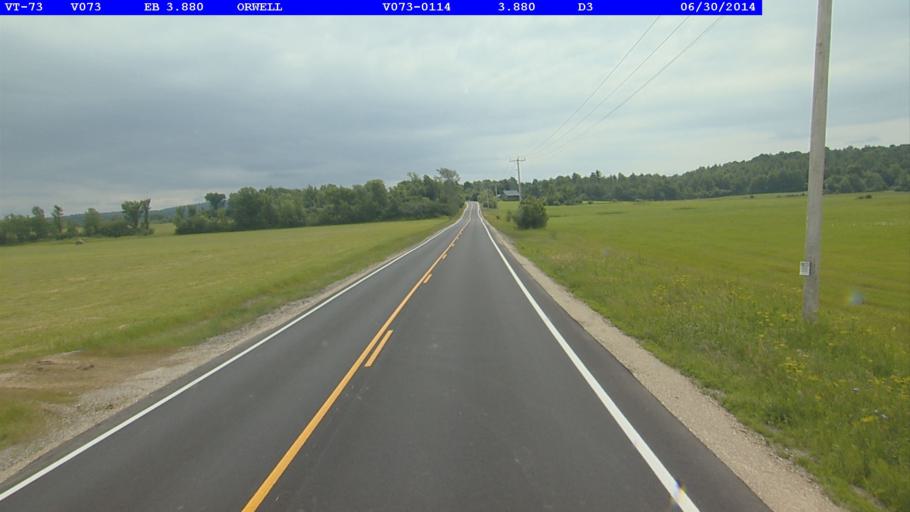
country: US
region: Vermont
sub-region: Rutland County
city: Brandon
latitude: 43.7972
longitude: -73.2325
